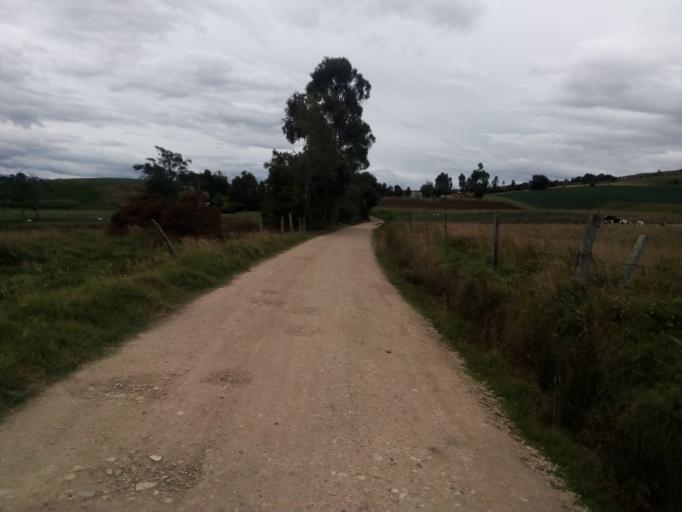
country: CO
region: Boyaca
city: Toca
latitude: 5.5842
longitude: -73.1423
